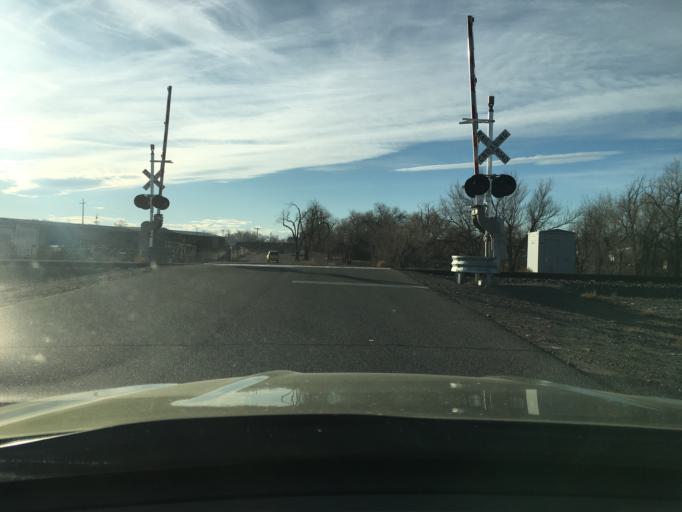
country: US
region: Colorado
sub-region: Delta County
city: Delta
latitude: 38.7458
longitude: -108.0786
